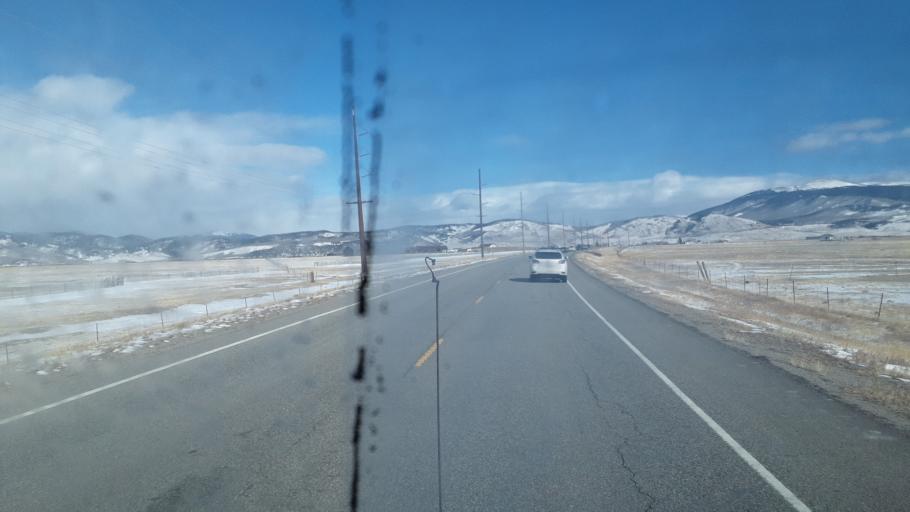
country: US
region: Colorado
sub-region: Park County
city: Fairplay
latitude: 39.3671
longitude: -105.8117
